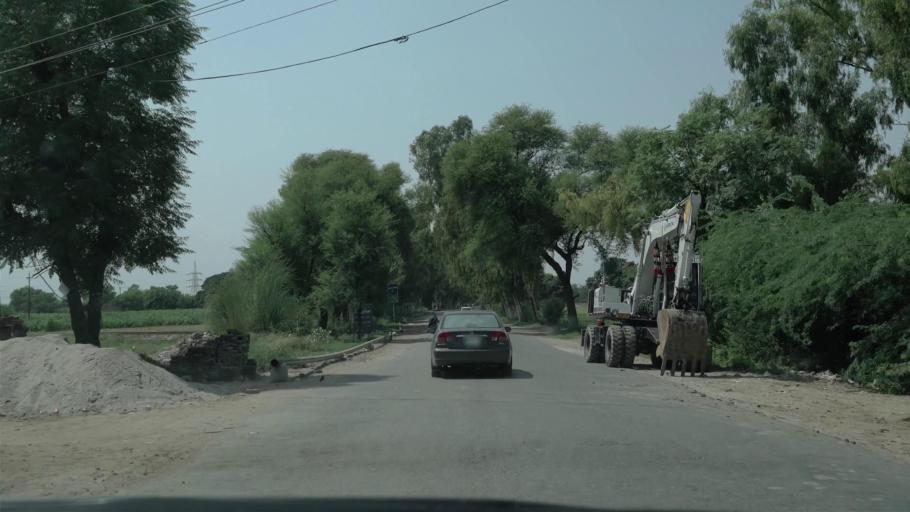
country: PK
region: Punjab
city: Gojra
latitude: 31.1699
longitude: 72.6223
